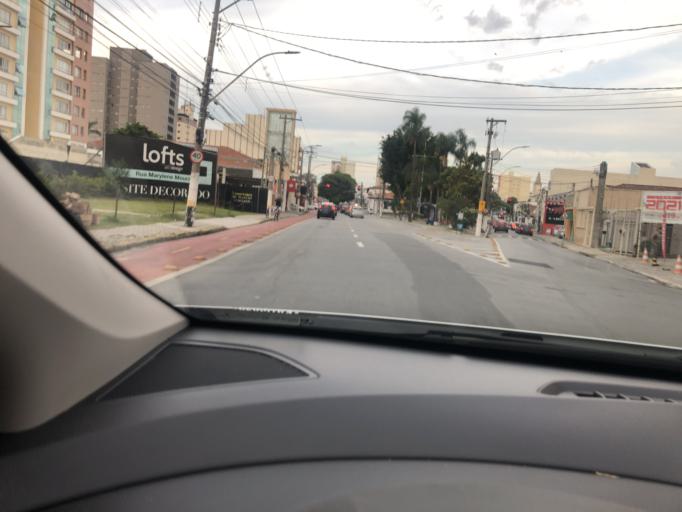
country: BR
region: Sao Paulo
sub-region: Taubate
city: Taubate
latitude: -23.0297
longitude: -45.5610
